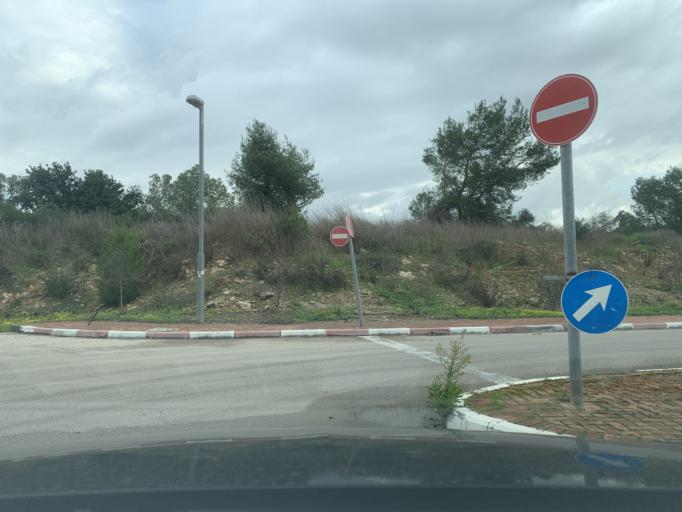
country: PS
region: West Bank
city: Qalqilyah
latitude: 32.2089
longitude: 34.9805
